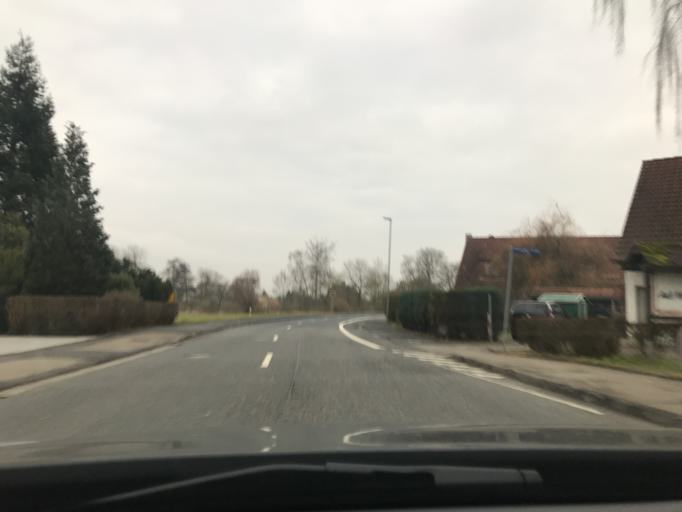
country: DE
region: Hesse
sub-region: Regierungsbezirk Kassel
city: Vellmar
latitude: 51.3463
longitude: 9.4814
